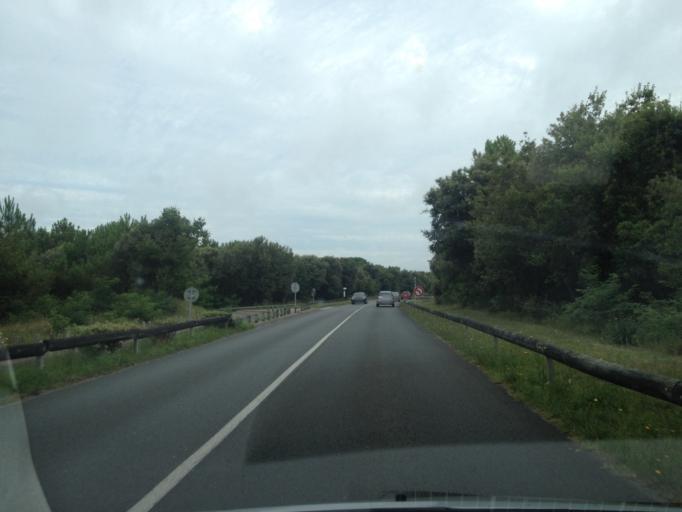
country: FR
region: Poitou-Charentes
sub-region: Departement de la Charente-Maritime
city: Les Mathes
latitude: 45.6696
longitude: -1.1434
